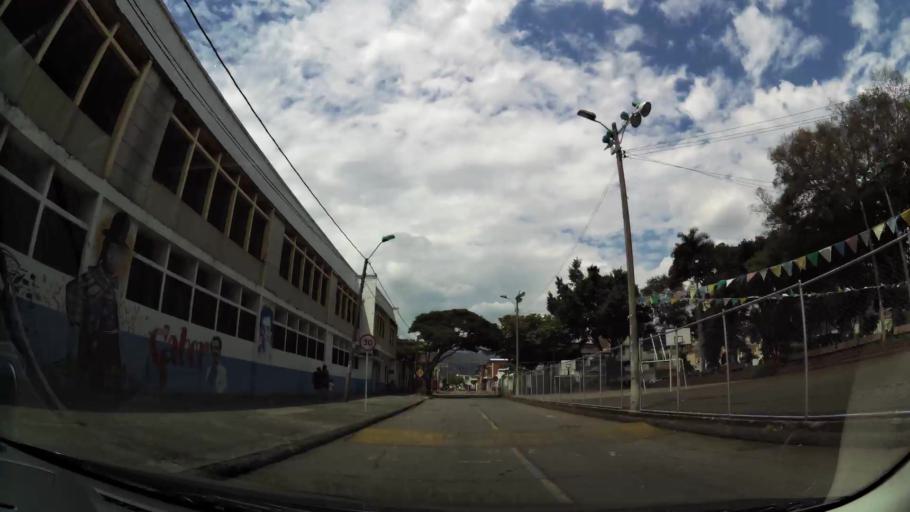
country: CO
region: Valle del Cauca
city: Cali
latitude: 3.4490
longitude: -76.5203
